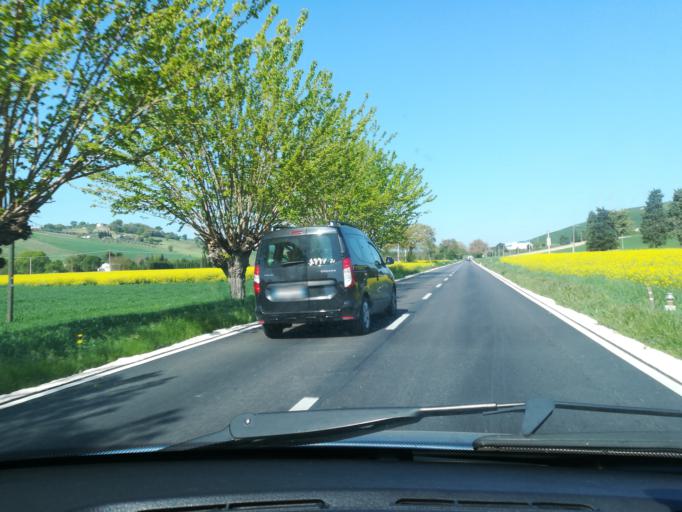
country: IT
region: The Marches
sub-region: Provincia di Macerata
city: Villa Potenza
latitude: 43.3271
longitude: 13.3996
